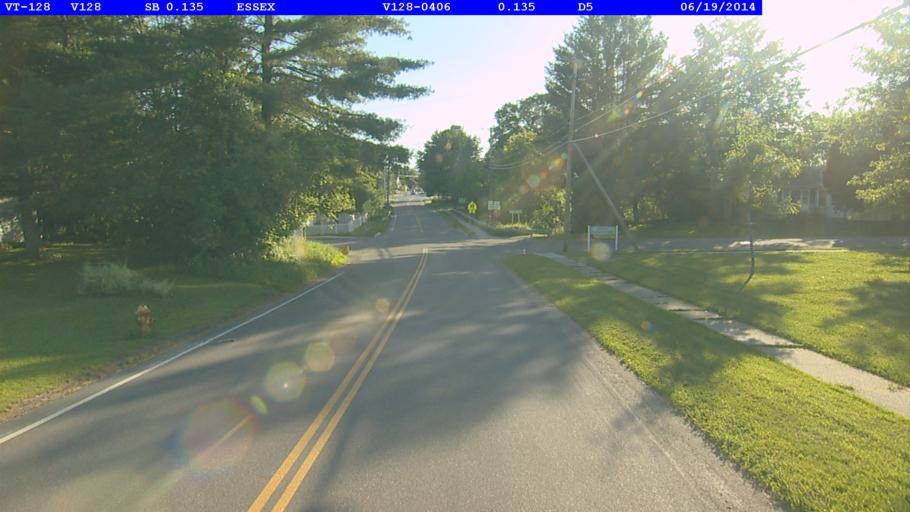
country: US
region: Vermont
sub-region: Chittenden County
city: Essex Junction
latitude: 44.5125
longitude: -73.0569
